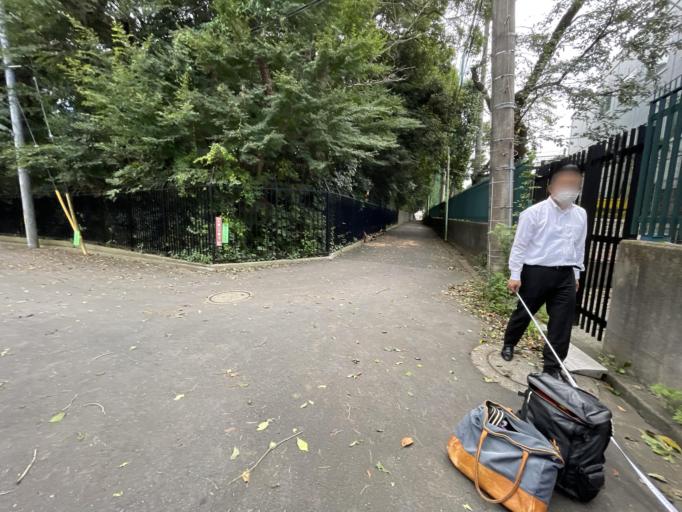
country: JP
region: Tokyo
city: Tokyo
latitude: 35.6832
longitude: 139.6391
